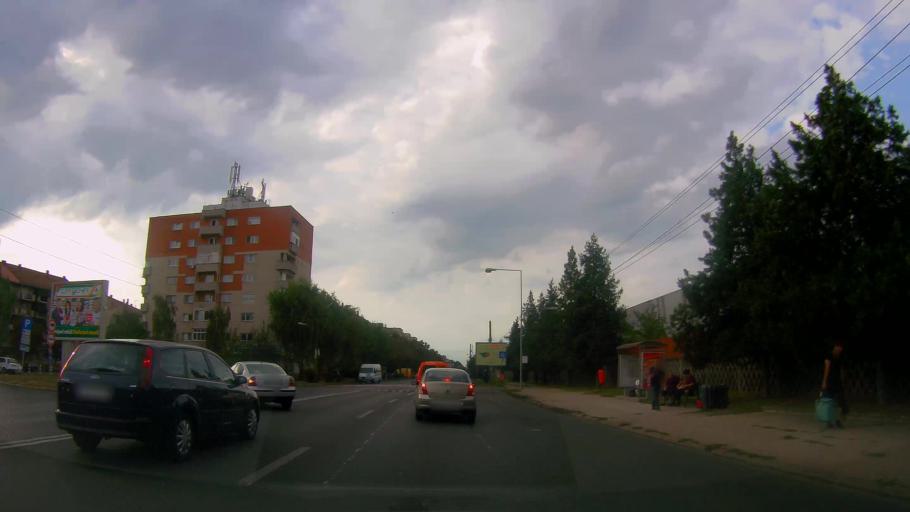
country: RO
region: Satu Mare
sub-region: Municipiul Satu Mare
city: Satu Mare
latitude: 47.7761
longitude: 22.8837
